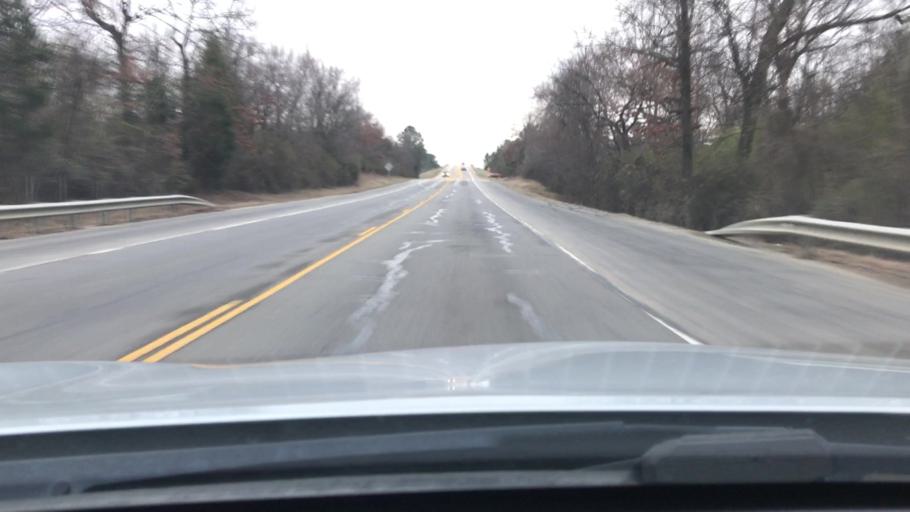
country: US
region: Arkansas
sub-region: Hempstead County
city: Hope
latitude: 33.6788
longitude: -93.5756
